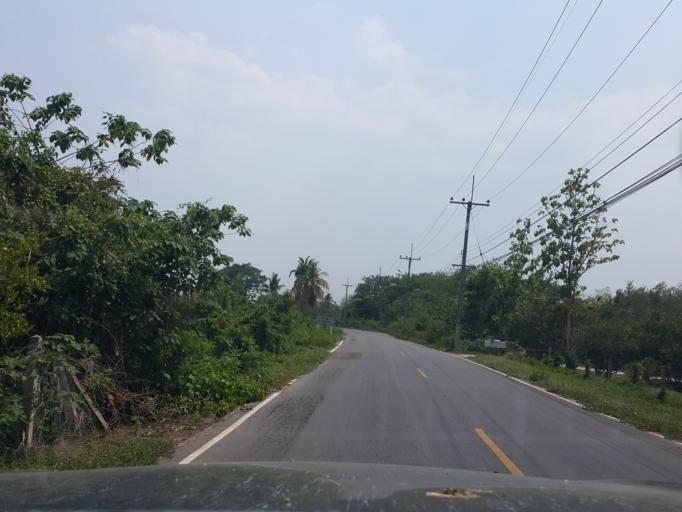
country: TH
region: Lampang
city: Mae Phrik
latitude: 17.5045
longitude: 99.1303
